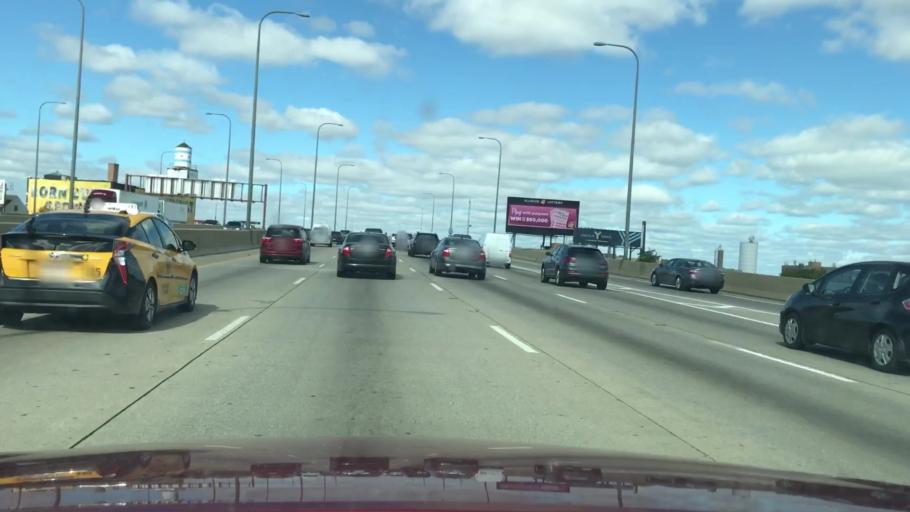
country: US
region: Illinois
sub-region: Cook County
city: Chicago
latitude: 41.9121
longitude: -87.6658
